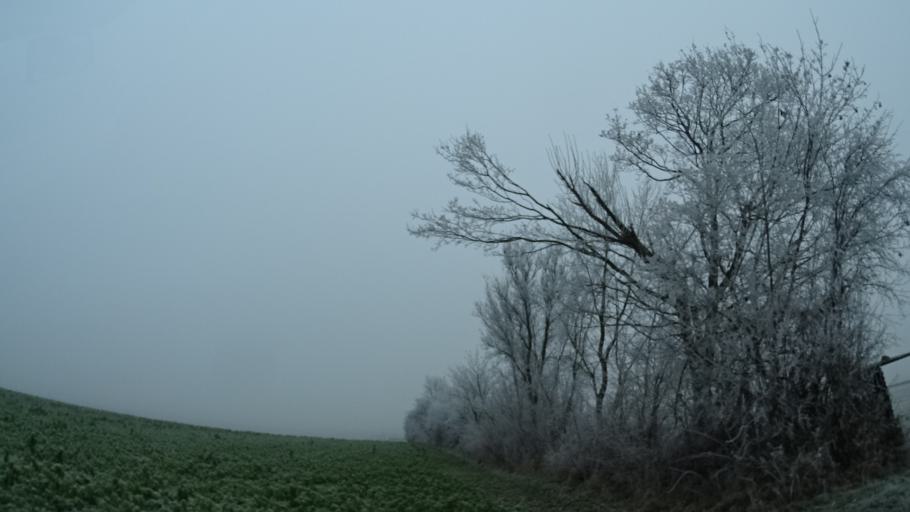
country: DE
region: Bavaria
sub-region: Regierungsbezirk Unterfranken
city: Lulsfeld
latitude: 49.8412
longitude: 10.2887
